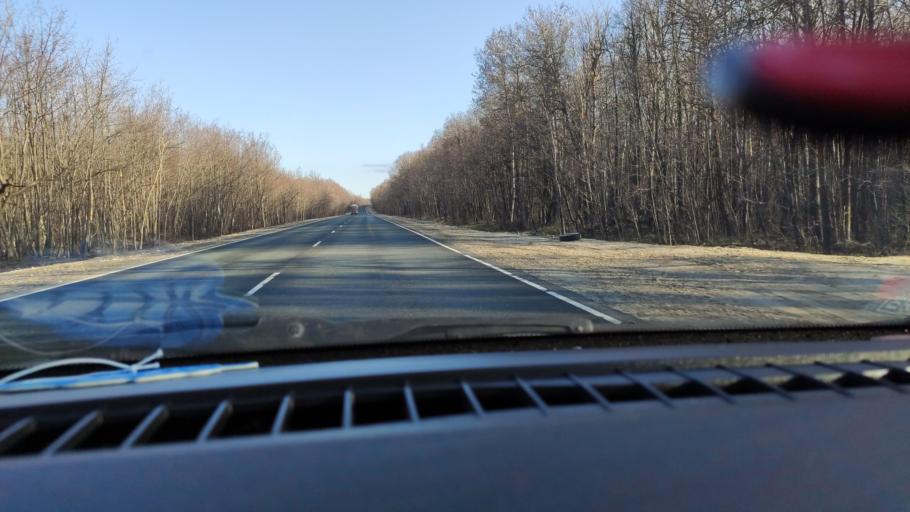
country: RU
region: Saratov
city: Khvalynsk
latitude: 52.4701
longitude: 48.0159
